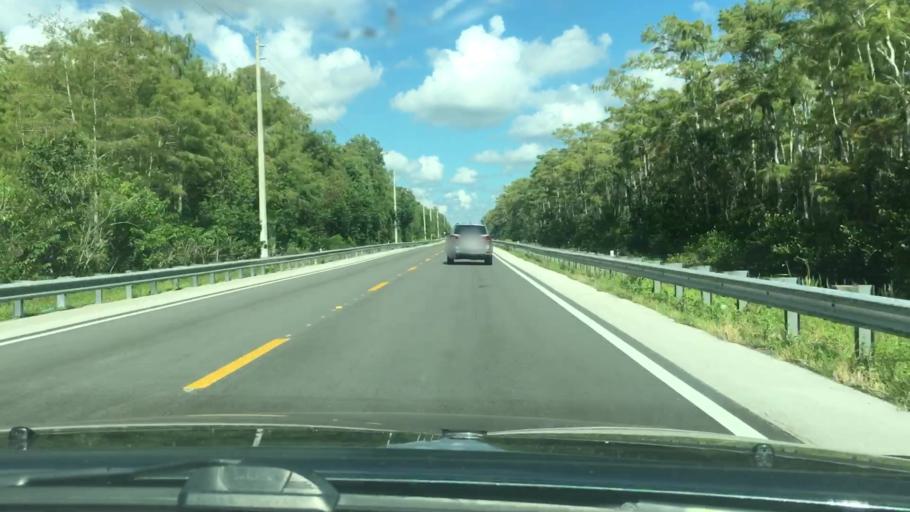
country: US
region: Florida
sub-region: Miami-Dade County
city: Kendall West
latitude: 25.8000
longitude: -80.8674
